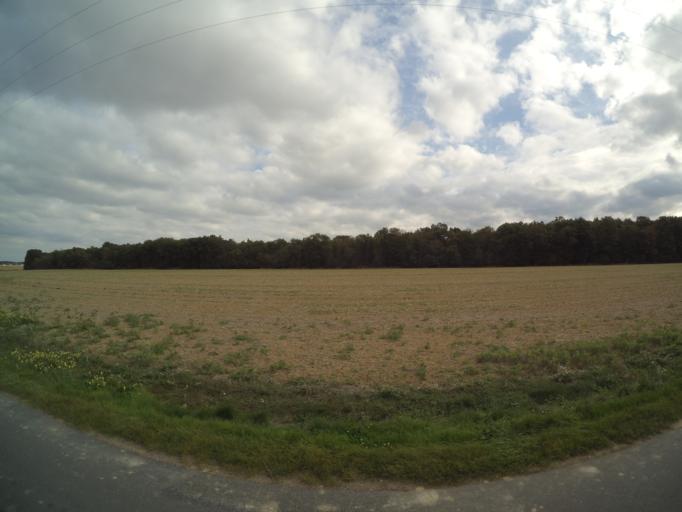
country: FR
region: Centre
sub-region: Departement d'Indre-et-Loire
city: Nazelles-Negron
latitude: 47.4720
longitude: 0.9414
